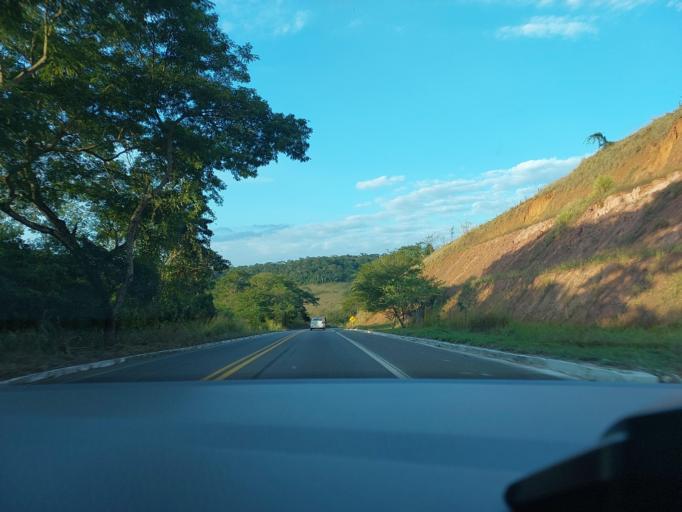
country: BR
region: Minas Gerais
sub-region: Muriae
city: Muriae
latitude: -21.1221
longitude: -42.2144
